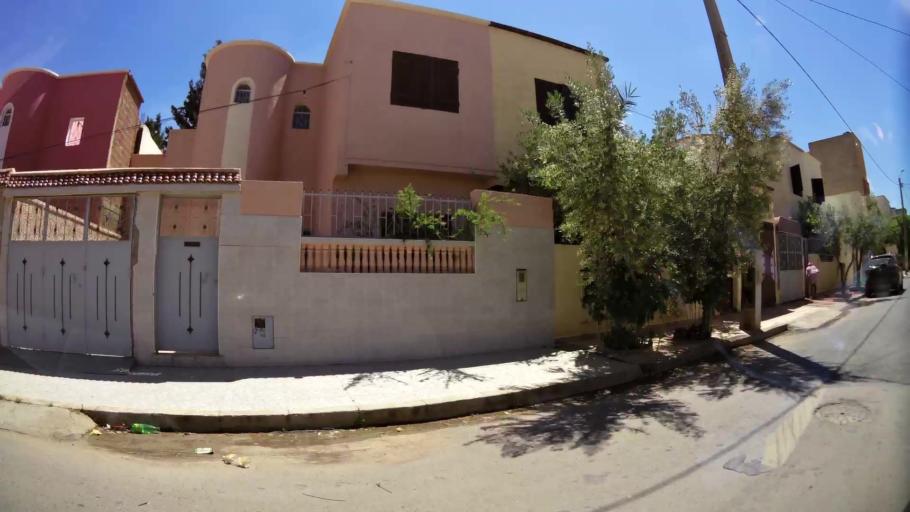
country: MA
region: Oriental
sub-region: Oujda-Angad
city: Oujda
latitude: 34.6588
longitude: -1.9384
